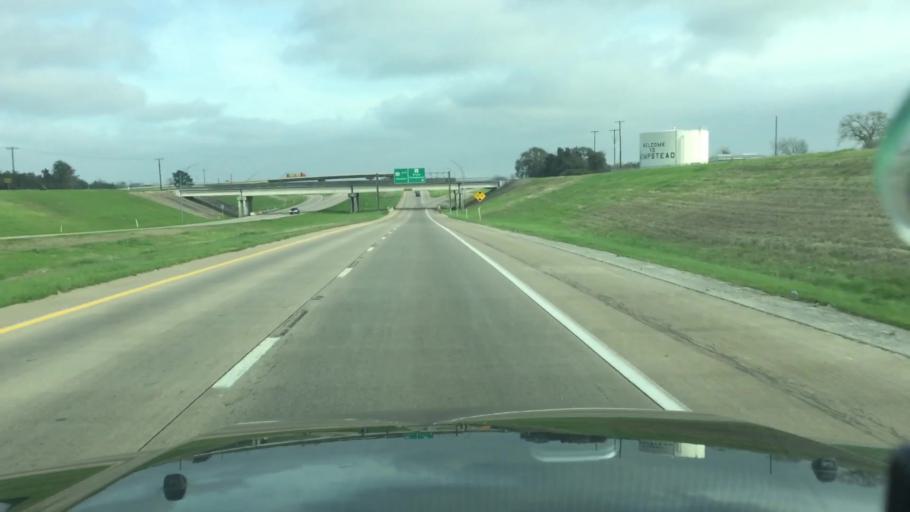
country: US
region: Texas
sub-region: Waller County
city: Hempstead
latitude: 30.1159
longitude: -96.0830
